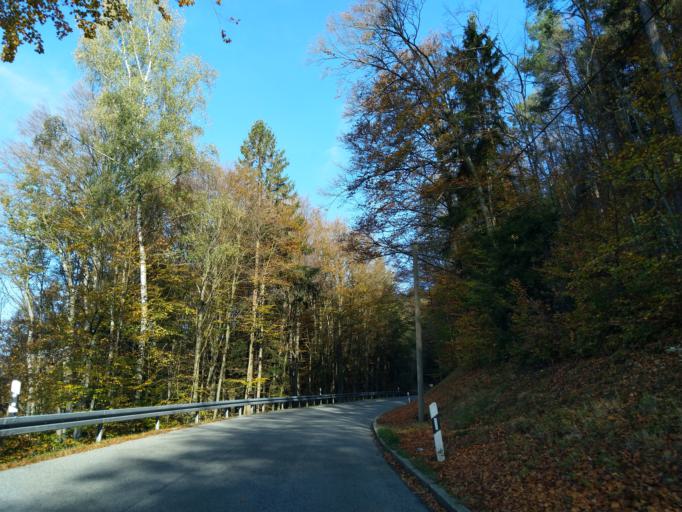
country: DE
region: Bavaria
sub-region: Lower Bavaria
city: Lalling
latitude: 48.8586
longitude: 13.1434
